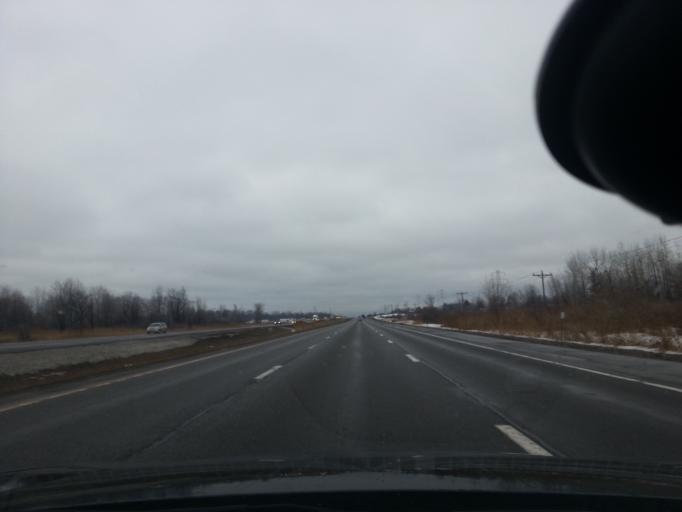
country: US
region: New York
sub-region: Onondaga County
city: Brewerton
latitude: 43.2070
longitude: -76.1279
